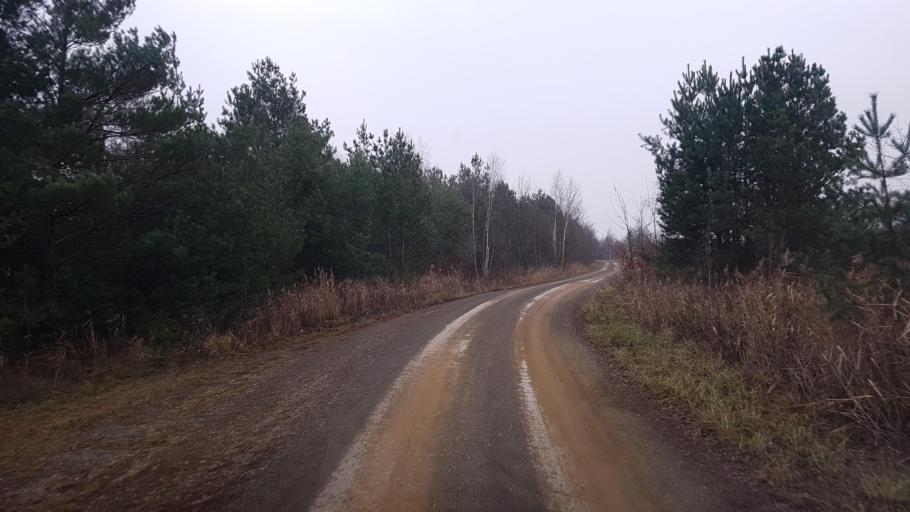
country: DE
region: Brandenburg
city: Plessa
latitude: 51.5105
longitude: 13.6557
